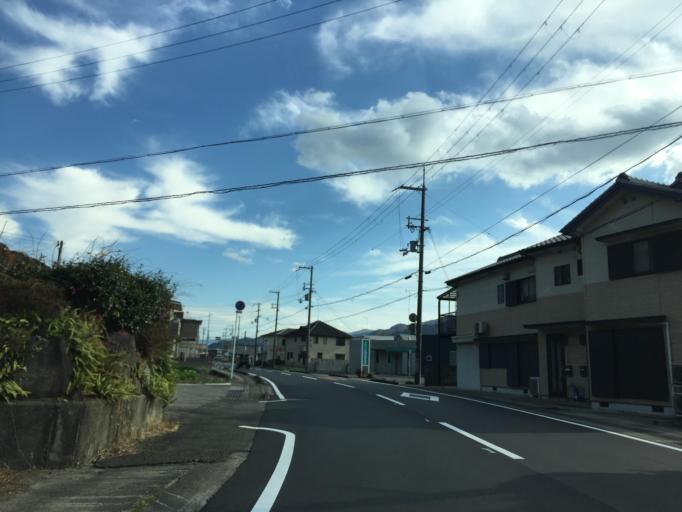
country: JP
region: Wakayama
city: Kainan
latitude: 34.1623
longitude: 135.2581
